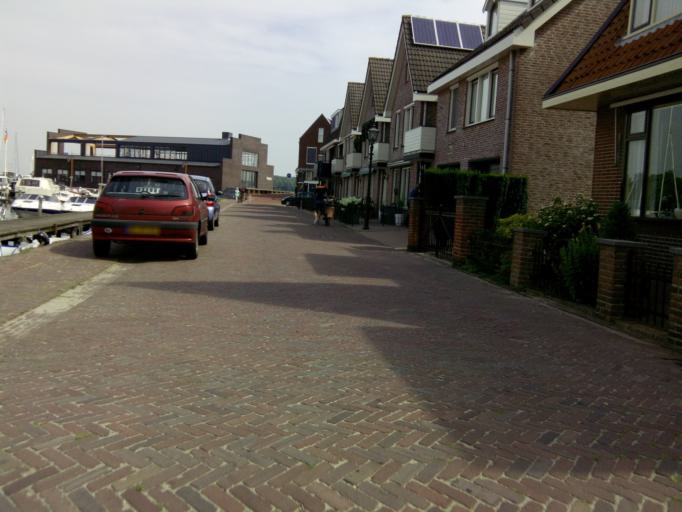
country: NL
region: Utrecht
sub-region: Gemeente Bunschoten
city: Bunschoten
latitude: 52.2552
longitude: 5.3820
